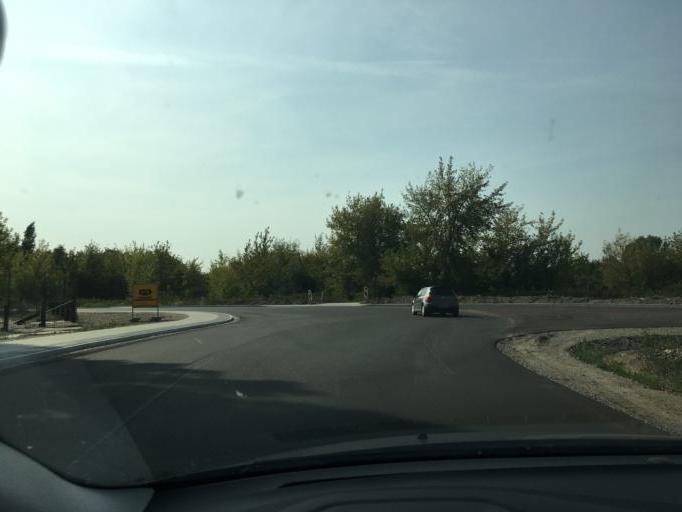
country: DE
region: Saxony-Anhalt
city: Calbe
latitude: 51.9187
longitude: 11.7916
